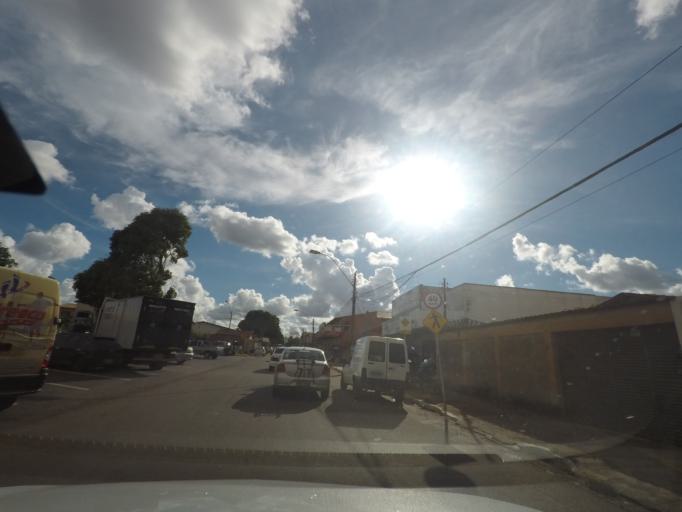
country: BR
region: Goias
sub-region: Goiania
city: Goiania
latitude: -16.7211
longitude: -49.3037
